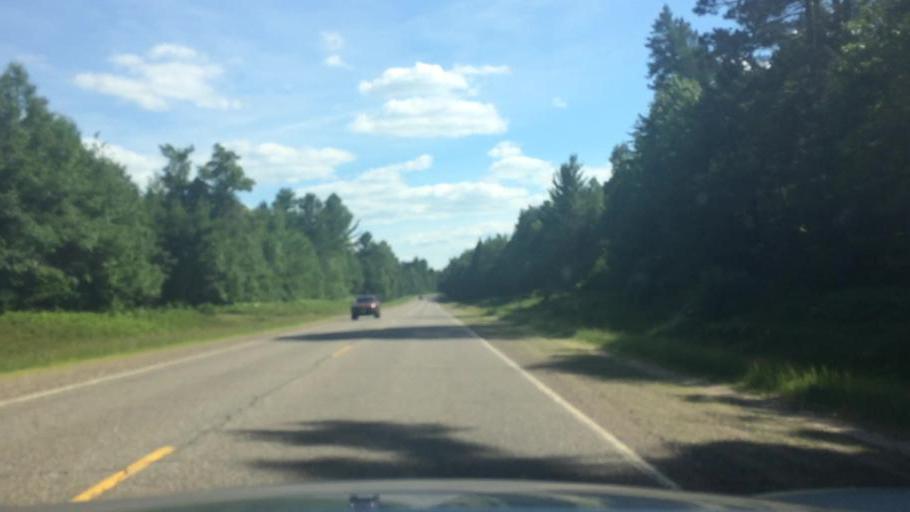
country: US
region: Wisconsin
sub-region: Vilas County
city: Lac du Flambeau
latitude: 46.0696
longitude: -89.6446
